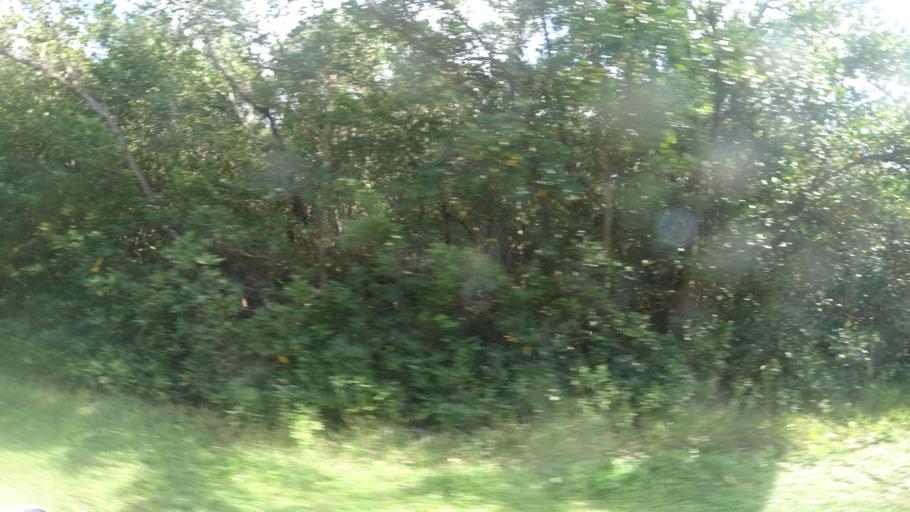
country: US
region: Florida
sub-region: Manatee County
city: Memphis
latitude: 27.5703
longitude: -82.5738
